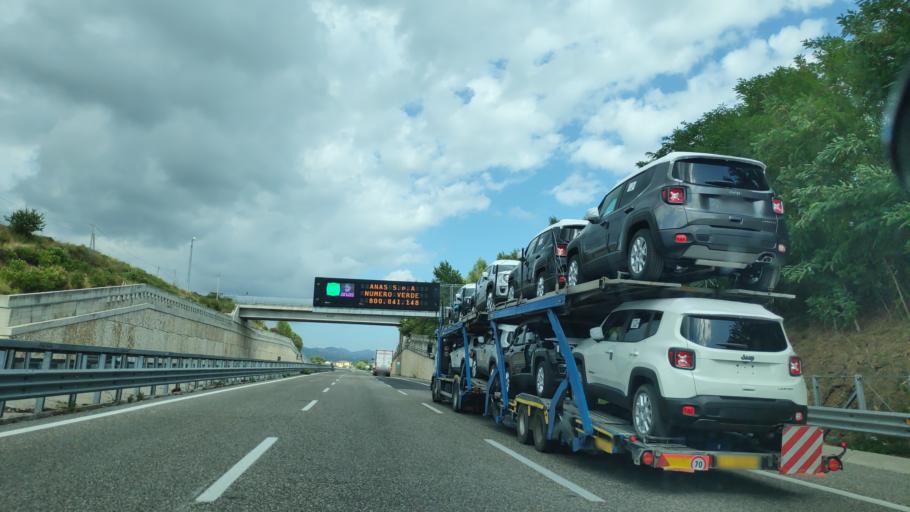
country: IT
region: Campania
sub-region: Provincia di Salerno
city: Contursi Terme
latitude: 40.6140
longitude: 15.2672
